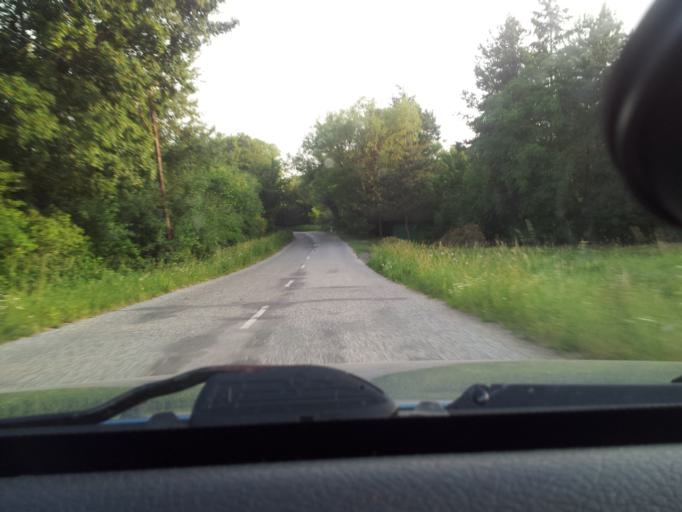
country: SK
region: Banskobystricky
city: Nova Bana
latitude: 48.3657
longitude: 18.7320
